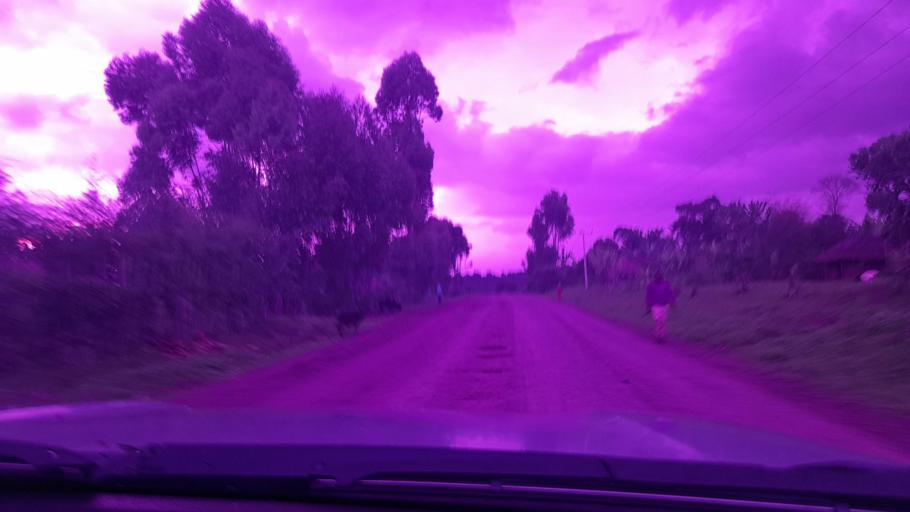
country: ET
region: Southern Nations, Nationalities, and People's Region
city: Mizan Teferi
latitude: 6.8996
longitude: 35.8413
